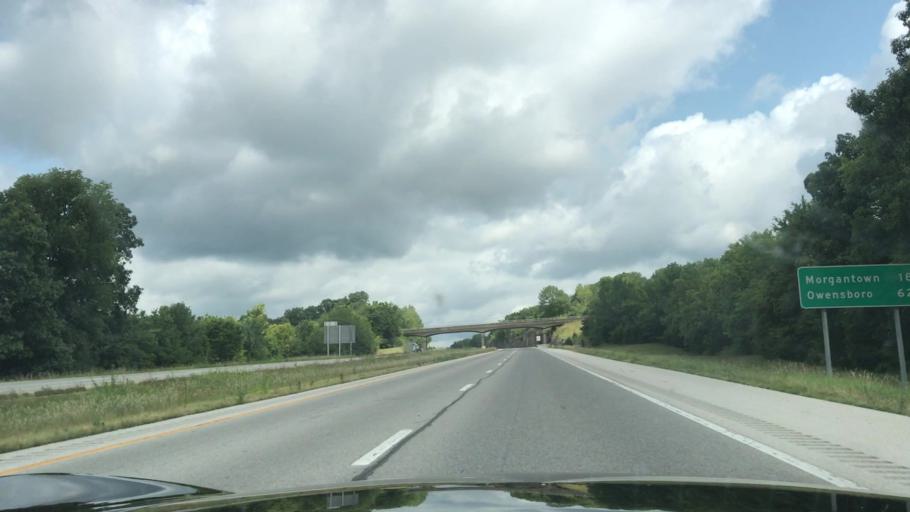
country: US
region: Kentucky
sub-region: Warren County
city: Bowling Green
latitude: 37.0000
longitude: -86.5059
